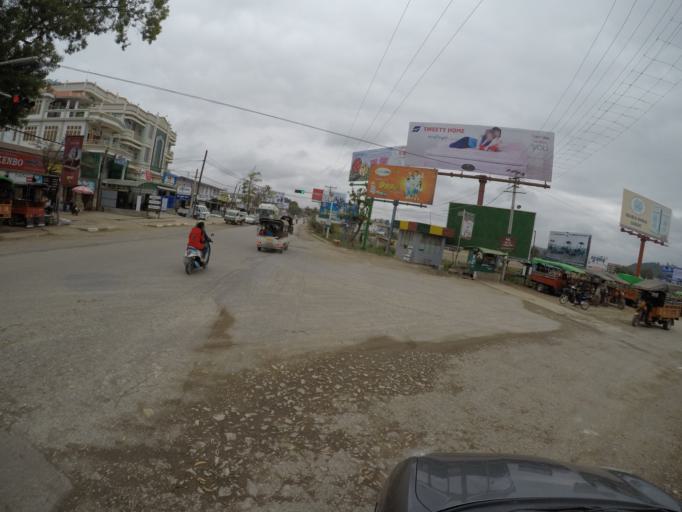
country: MM
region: Shan
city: Taunggyi
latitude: 20.6546
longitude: 96.6289
